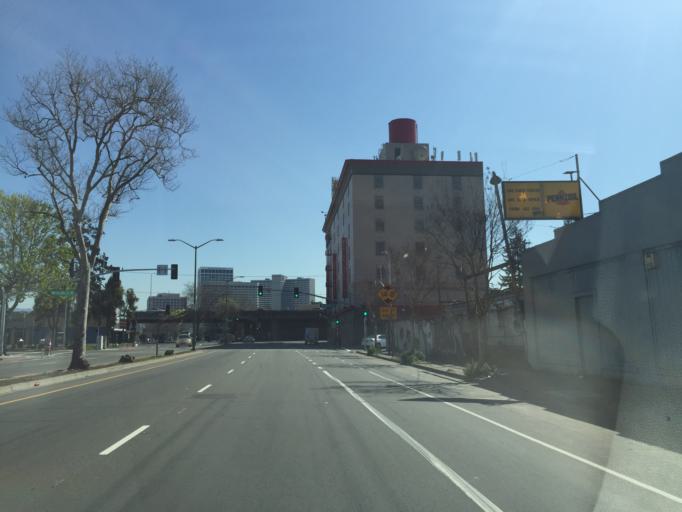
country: US
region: California
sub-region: Alameda County
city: Oakland
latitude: 37.8132
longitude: -122.2754
